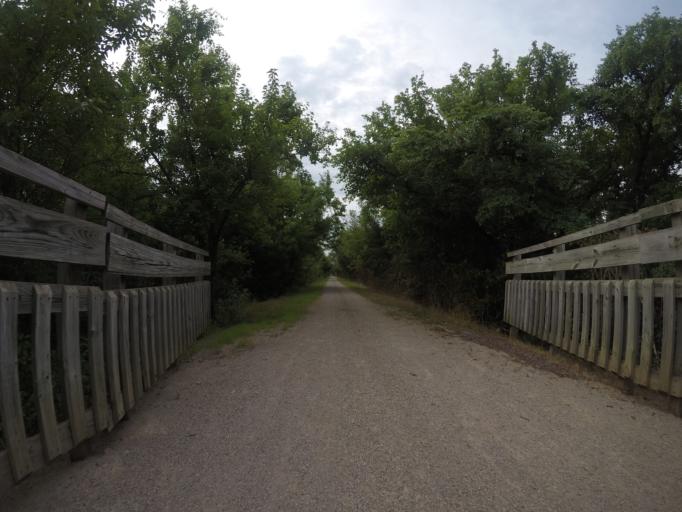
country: US
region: Kansas
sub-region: Franklin County
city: Ottawa
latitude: 38.4661
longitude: -95.2719
